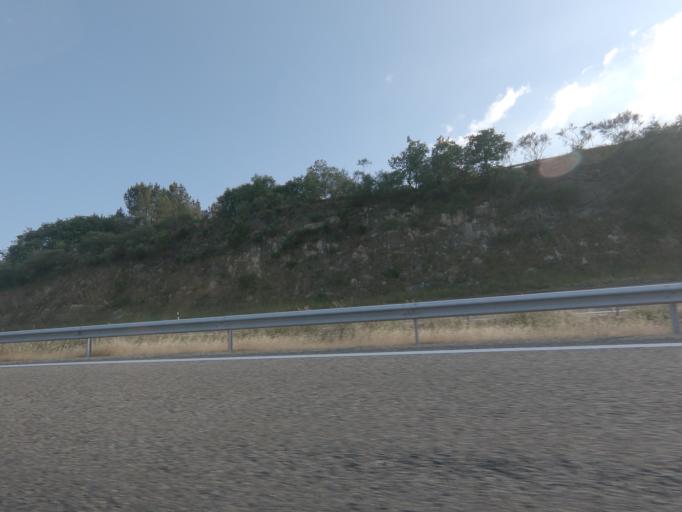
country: ES
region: Galicia
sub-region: Provincia de Ourense
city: Cualedro
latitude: 42.0039
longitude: -7.5644
